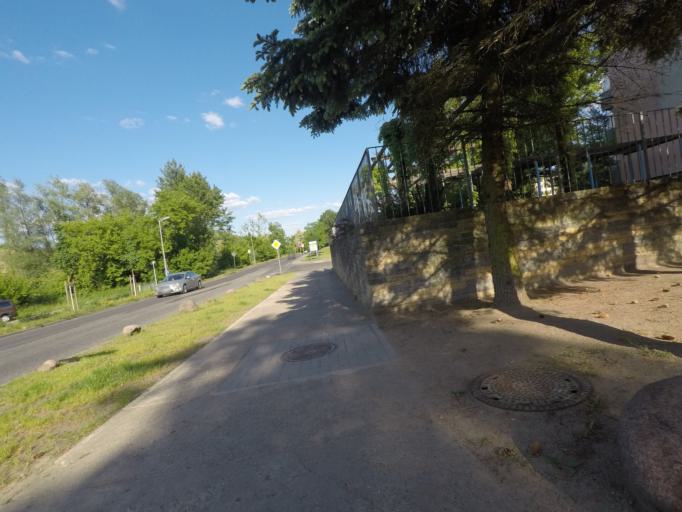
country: DE
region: Brandenburg
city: Eberswalde
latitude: 52.8407
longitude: 13.8127
